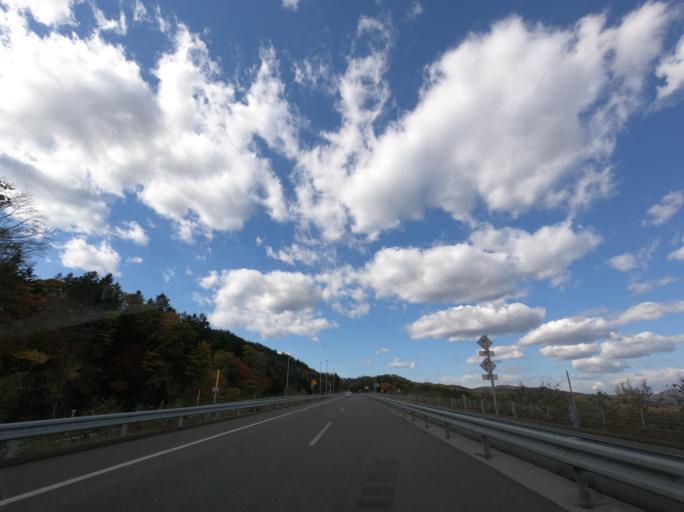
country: JP
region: Hokkaido
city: Kushiro
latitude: 43.0777
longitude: 144.0619
